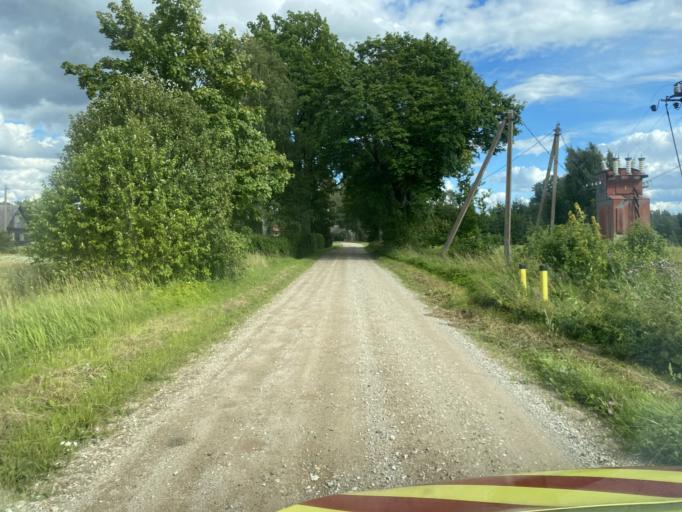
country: EE
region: Viljandimaa
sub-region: Viiratsi vald
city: Viiratsi
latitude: 58.3973
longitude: 25.8181
